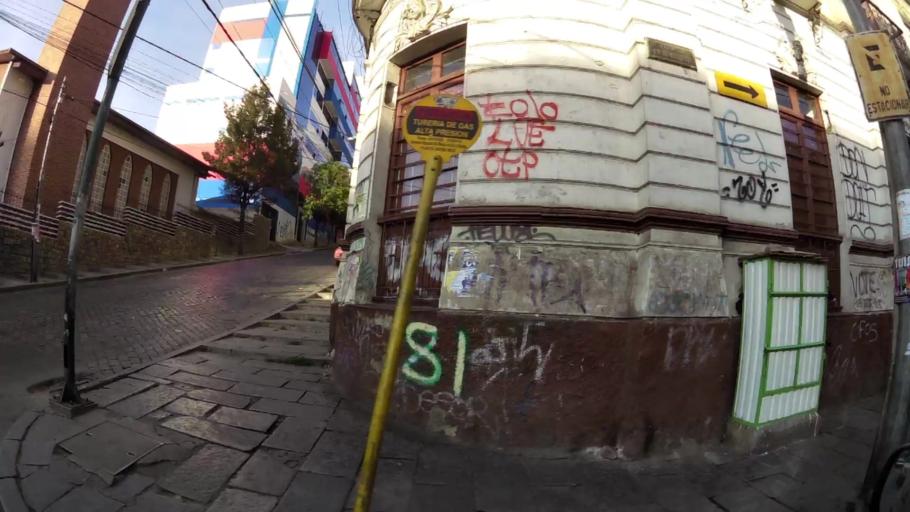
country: BO
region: La Paz
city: La Paz
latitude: -16.5053
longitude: -68.1319
